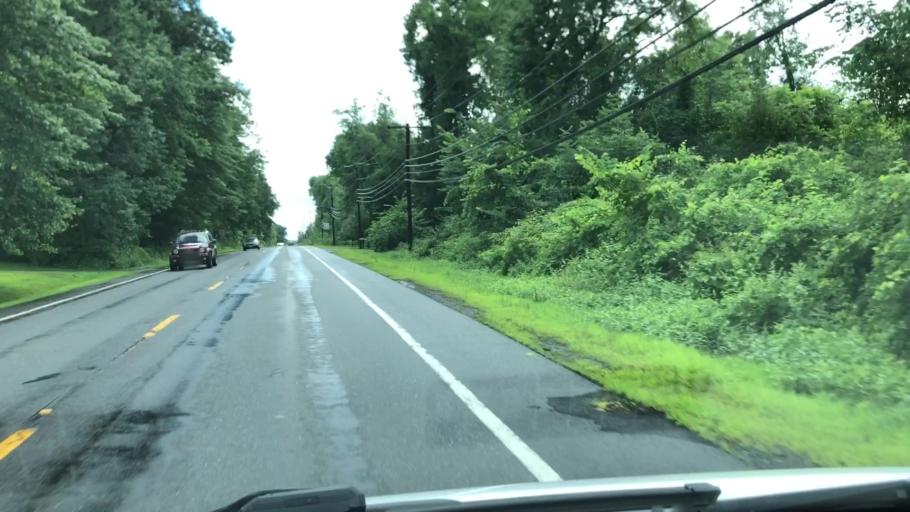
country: US
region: Massachusetts
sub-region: Franklin County
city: Greenfield
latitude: 42.5491
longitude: -72.6007
